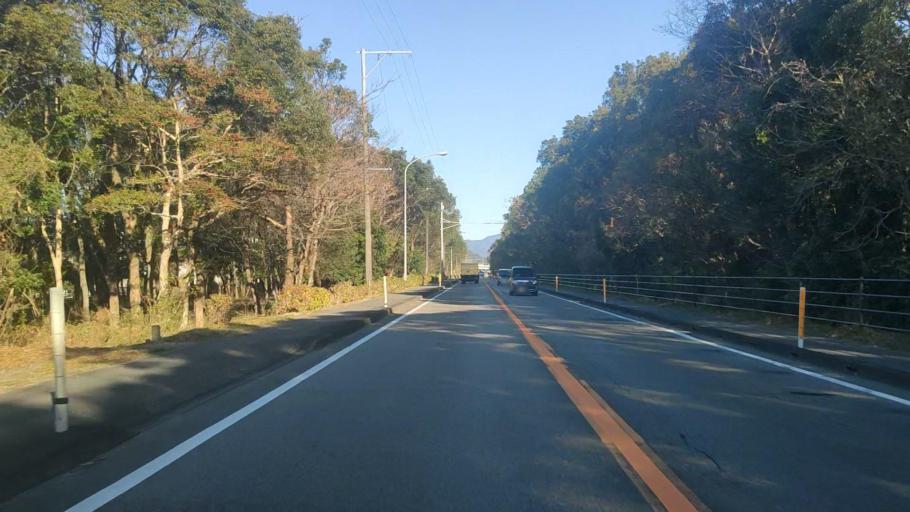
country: JP
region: Miyazaki
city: Nobeoka
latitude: 32.5310
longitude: 131.6811
